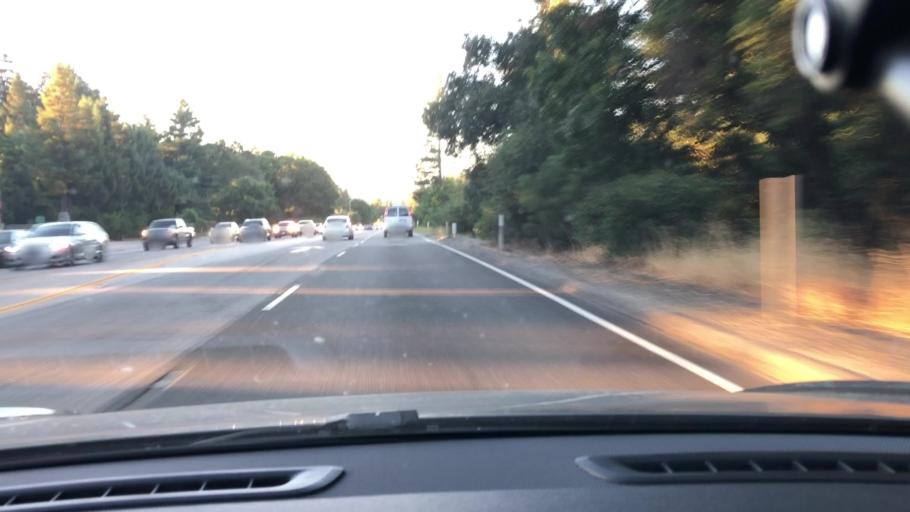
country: US
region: California
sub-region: Santa Clara County
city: Lexington Hills
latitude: 37.1330
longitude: -121.9814
